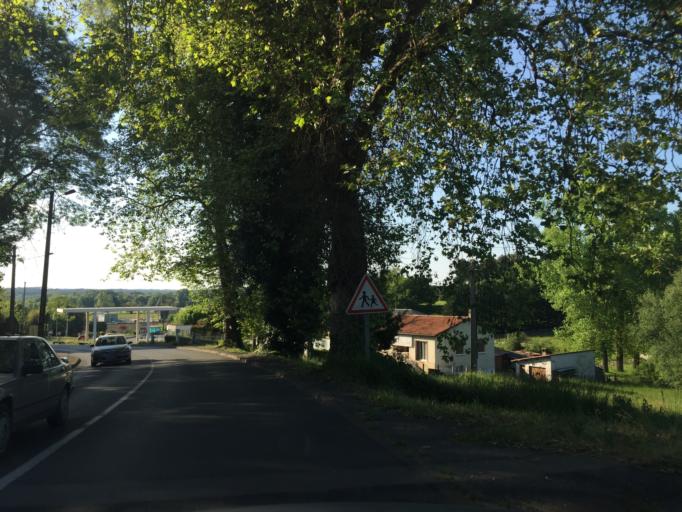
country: FR
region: Aquitaine
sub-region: Departement de la Dordogne
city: La Roche-Chalais
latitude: 45.1553
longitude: 0.0089
